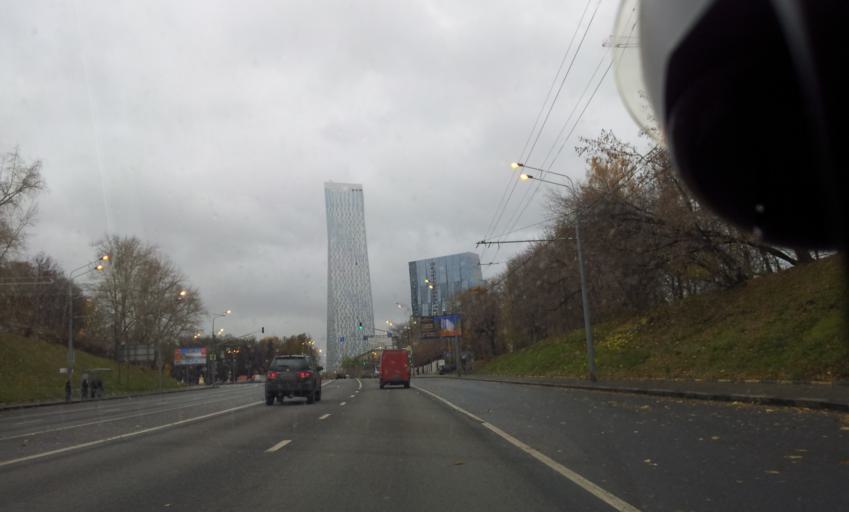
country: RU
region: Moscow
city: Vorob'yovo
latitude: 55.7277
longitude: 37.5381
